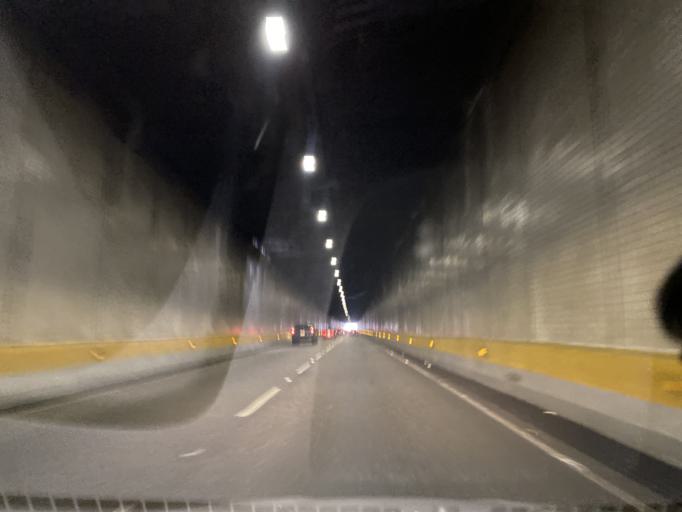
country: DO
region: Santo Domingo
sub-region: Santo Domingo
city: Santo Domingo Este
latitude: 18.4848
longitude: -69.8700
